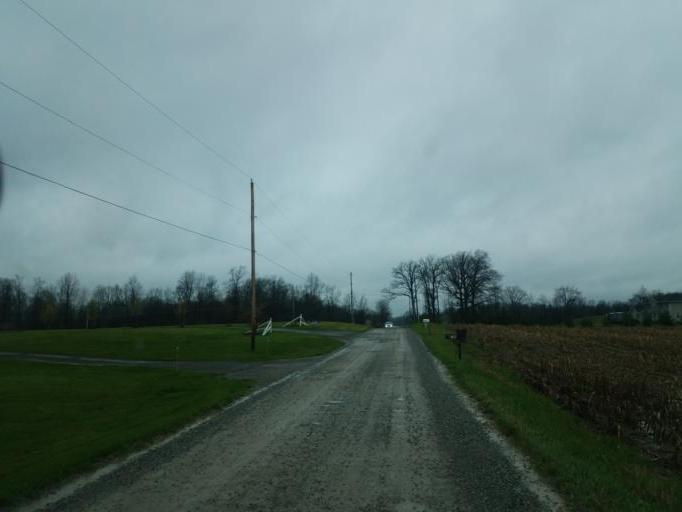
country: US
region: Ohio
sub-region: Morrow County
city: Mount Gilead
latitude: 40.4462
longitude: -82.7865
